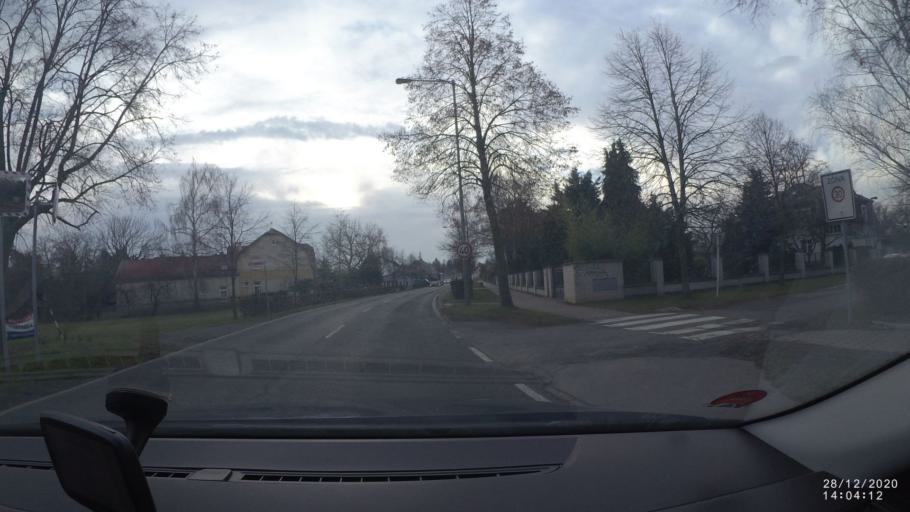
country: CZ
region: Central Bohemia
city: Sestajovice
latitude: 50.1006
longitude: 14.6740
